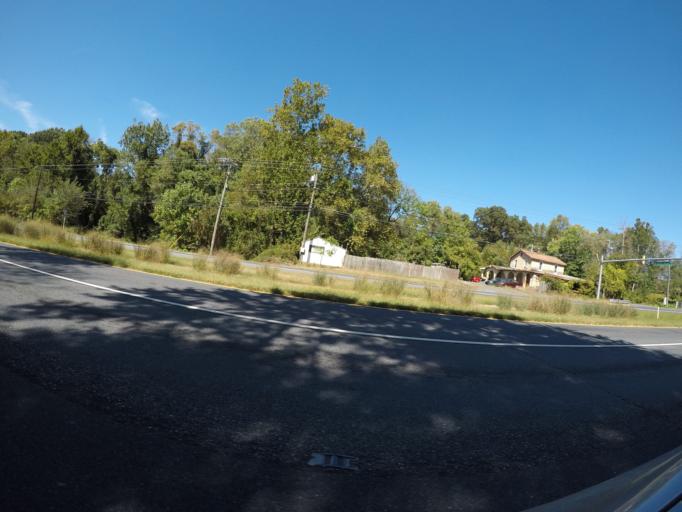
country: US
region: Maryland
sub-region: Harford County
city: Aberdeen
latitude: 39.5235
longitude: -76.1404
